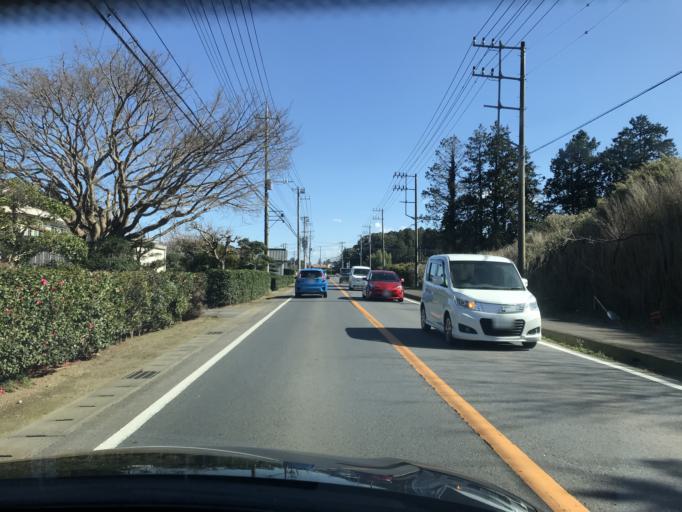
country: JP
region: Chiba
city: Sawara
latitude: 35.8383
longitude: 140.5464
